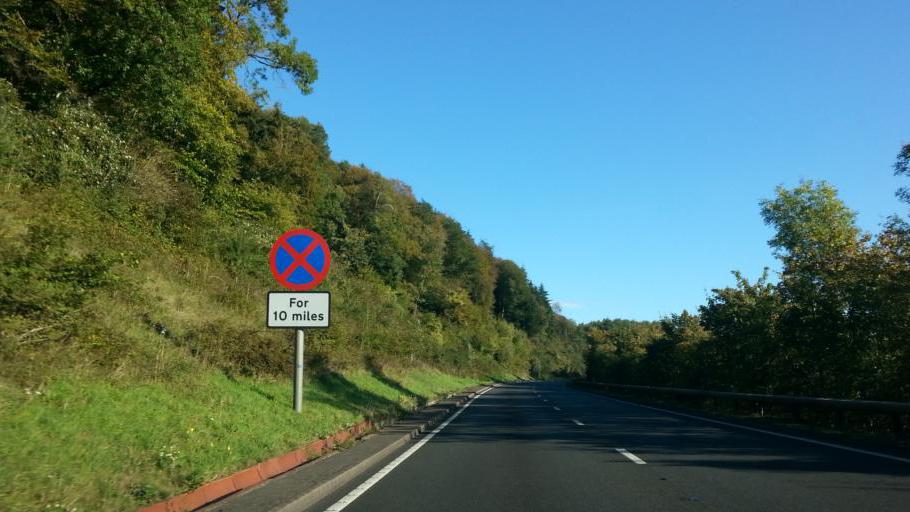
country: GB
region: Wales
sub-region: Monmouthshire
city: Monmouth
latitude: 51.8334
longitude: -2.6890
